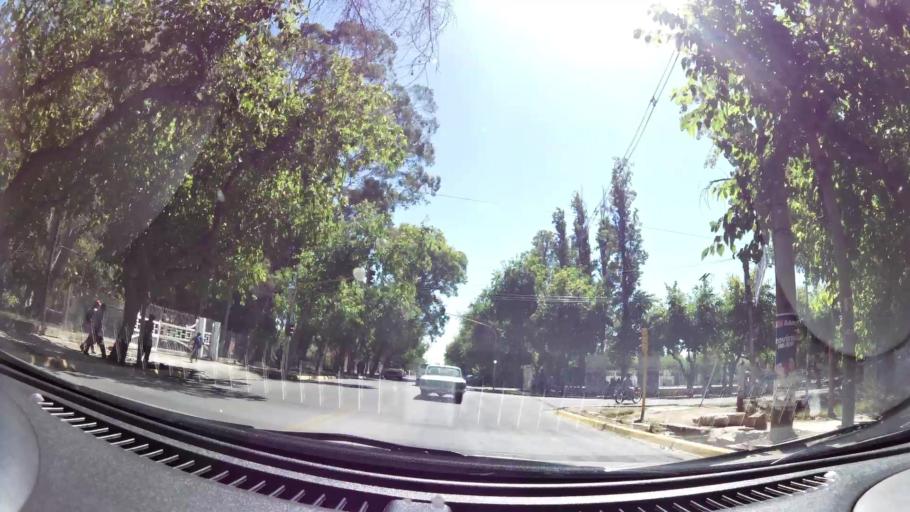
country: AR
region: San Juan
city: San Juan
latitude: -31.5286
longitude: -68.5544
